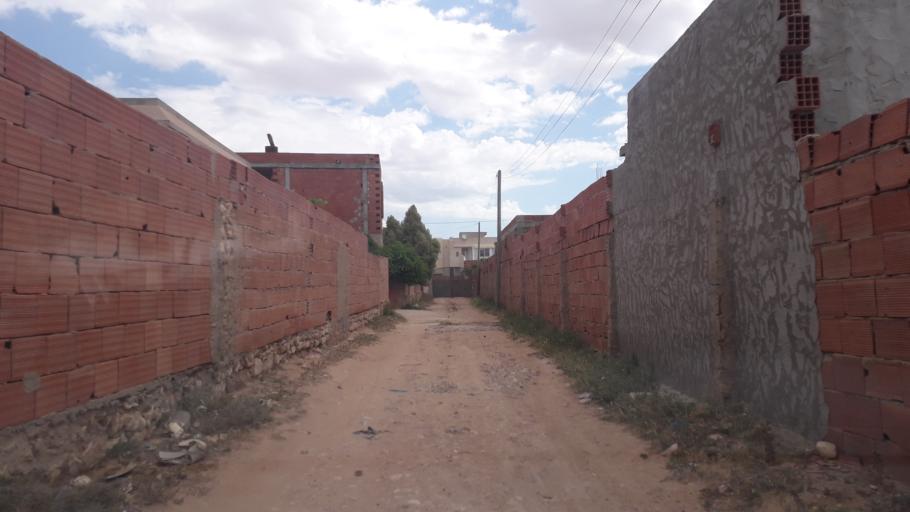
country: TN
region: Safaqis
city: Al Qarmadah
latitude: 34.8390
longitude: 10.7741
